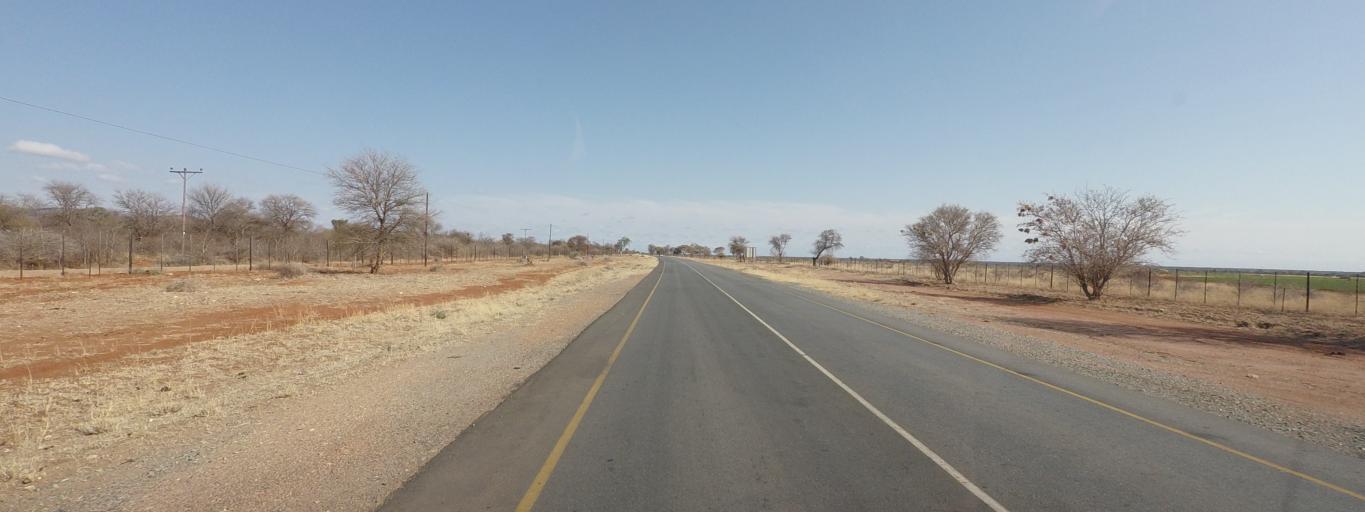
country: BW
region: Central
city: Makobeng
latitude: -22.9873
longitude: 27.9243
